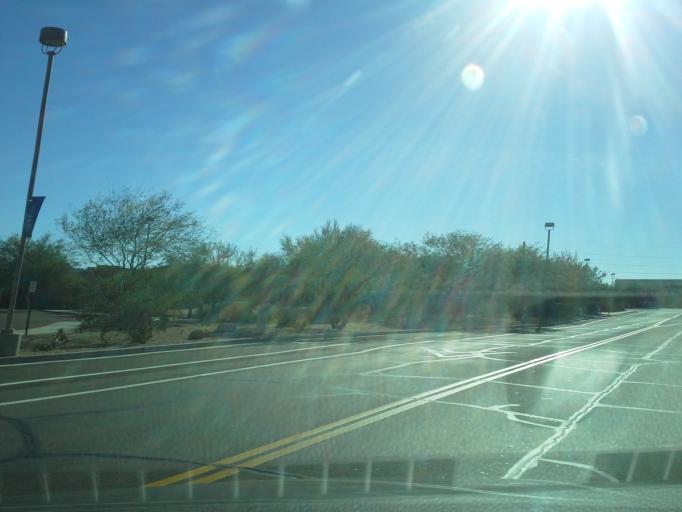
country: US
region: Arizona
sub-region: Maricopa County
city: Paradise Valley
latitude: 33.6573
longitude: -111.9583
